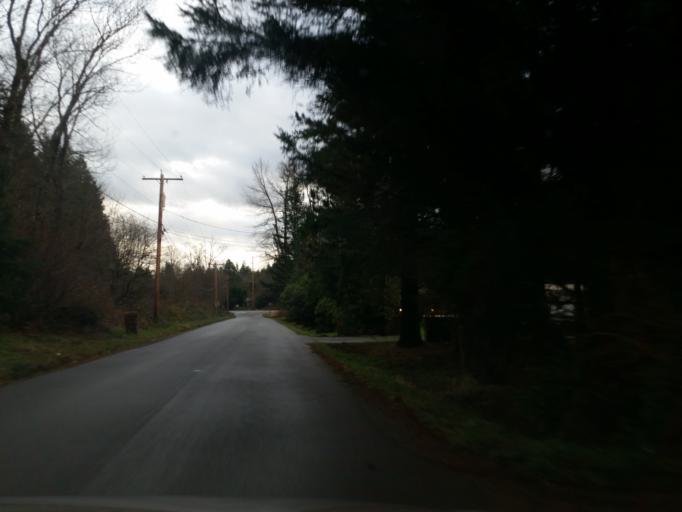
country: US
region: Washington
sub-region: King County
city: Snoqualmie
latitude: 47.5075
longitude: -121.8103
